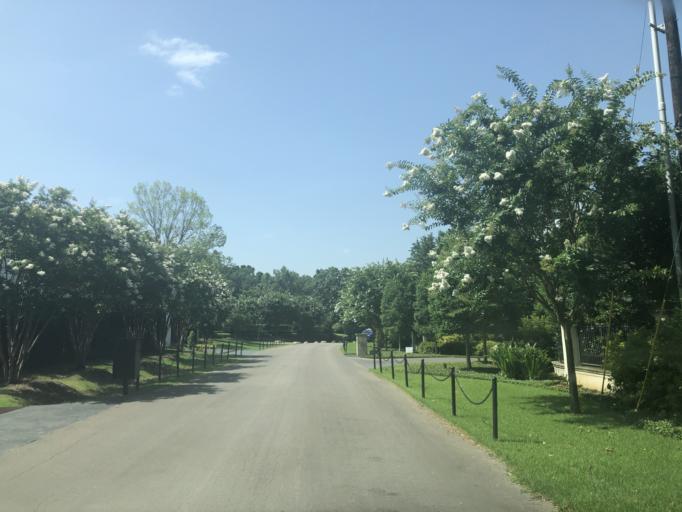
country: US
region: Texas
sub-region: Dallas County
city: University Park
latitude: 32.8779
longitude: -96.8169
